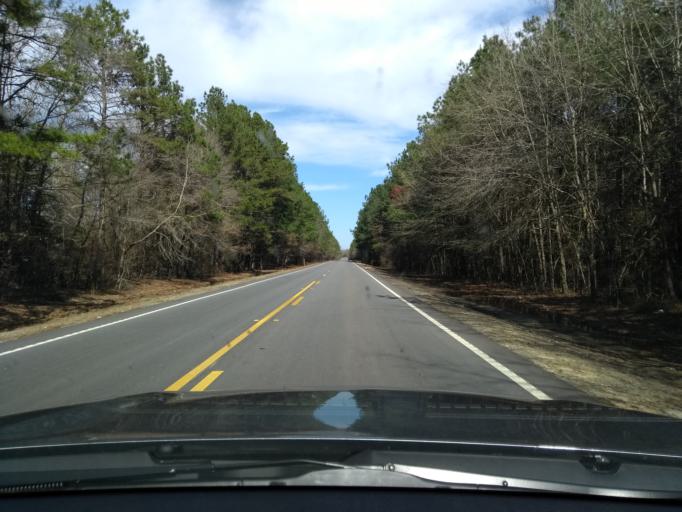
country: US
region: Georgia
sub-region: Bulloch County
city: Brooklet
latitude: 32.4857
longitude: -81.5730
